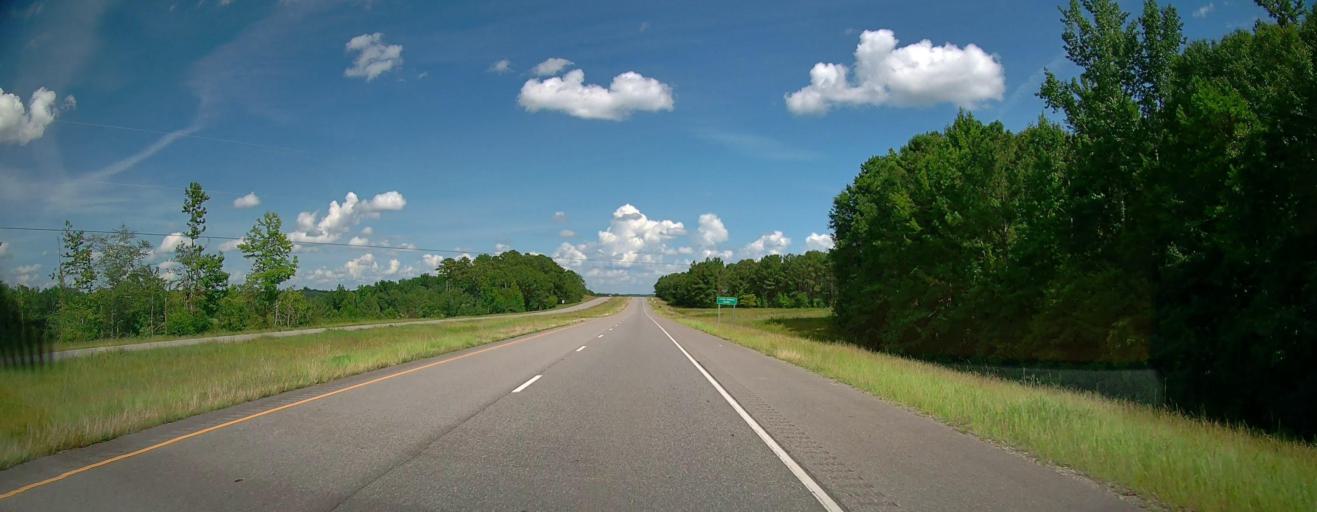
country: US
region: Alabama
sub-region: Pickens County
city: Reform
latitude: 33.3940
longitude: -88.0513
